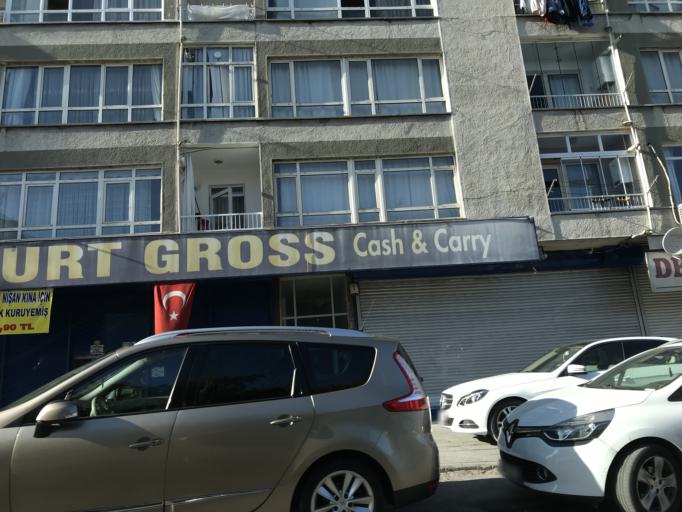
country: TR
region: Ankara
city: Cankaya
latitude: 39.9371
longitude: 32.8697
